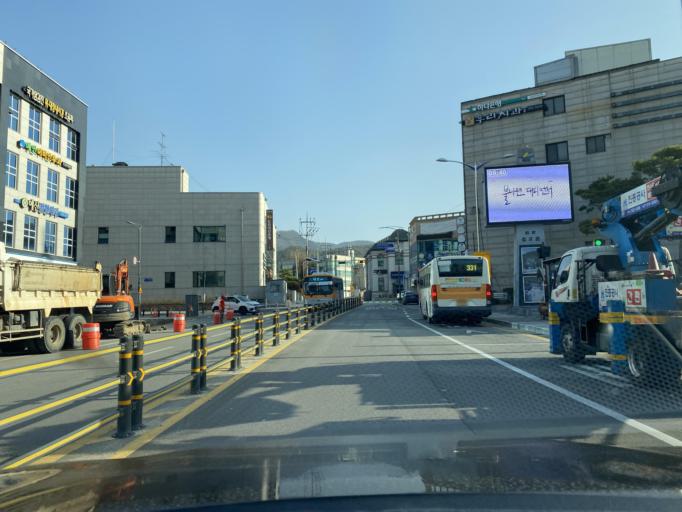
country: KR
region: Chungcheongnam-do
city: Yesan
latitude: 36.6795
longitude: 126.8464
